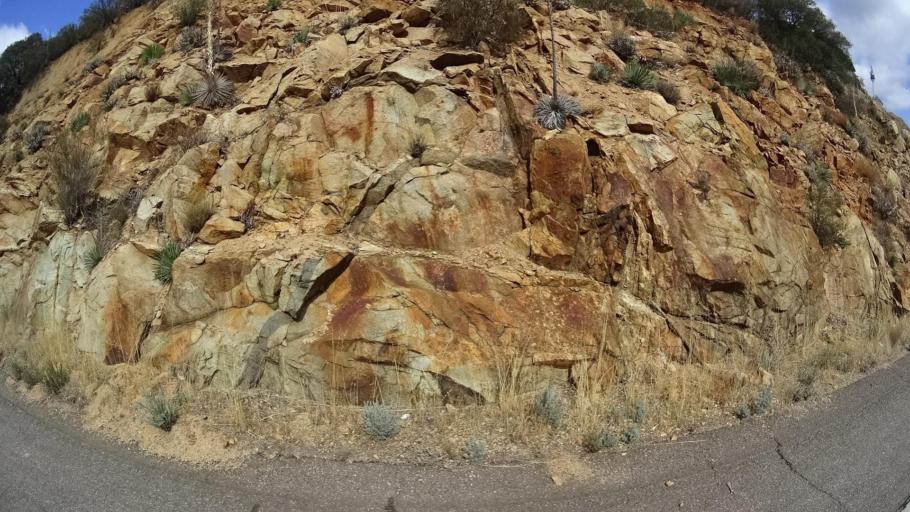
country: US
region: California
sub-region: San Diego County
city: Pine Valley
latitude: 32.7877
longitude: -116.4971
